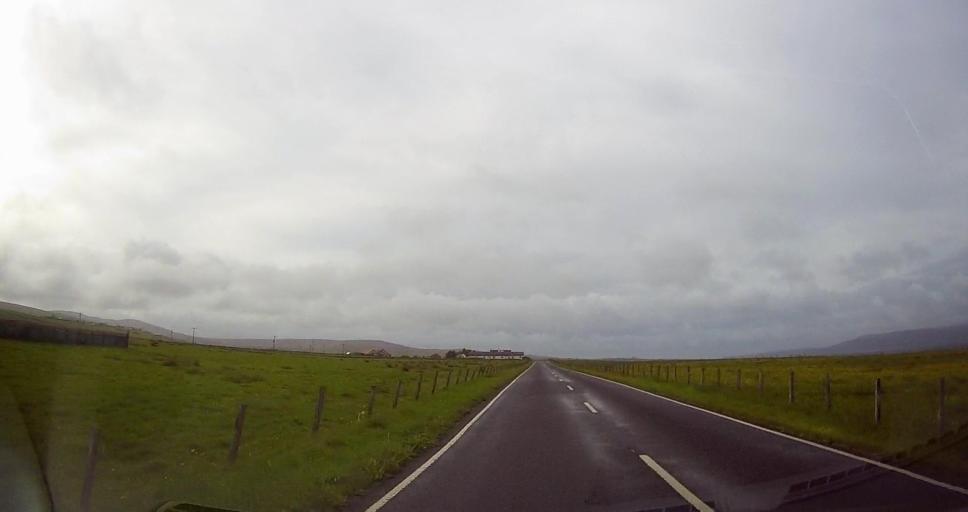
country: GB
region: Scotland
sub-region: Orkney Islands
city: Stromness
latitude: 58.9765
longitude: -3.2413
